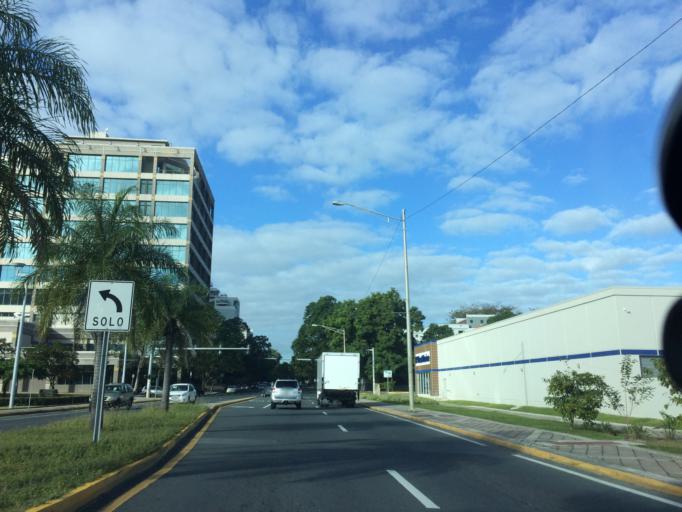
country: PR
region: San Juan
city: San Juan
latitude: 18.4291
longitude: -66.0620
